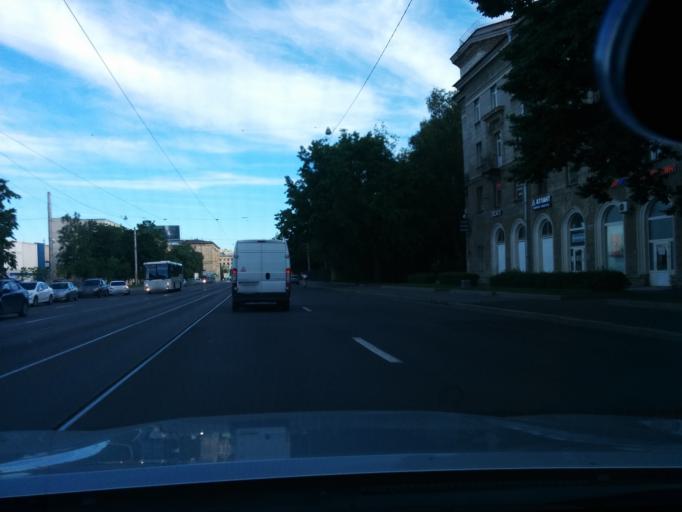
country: RU
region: Leningrad
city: Svetlanovskiy
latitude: 60.0078
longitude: 30.3259
